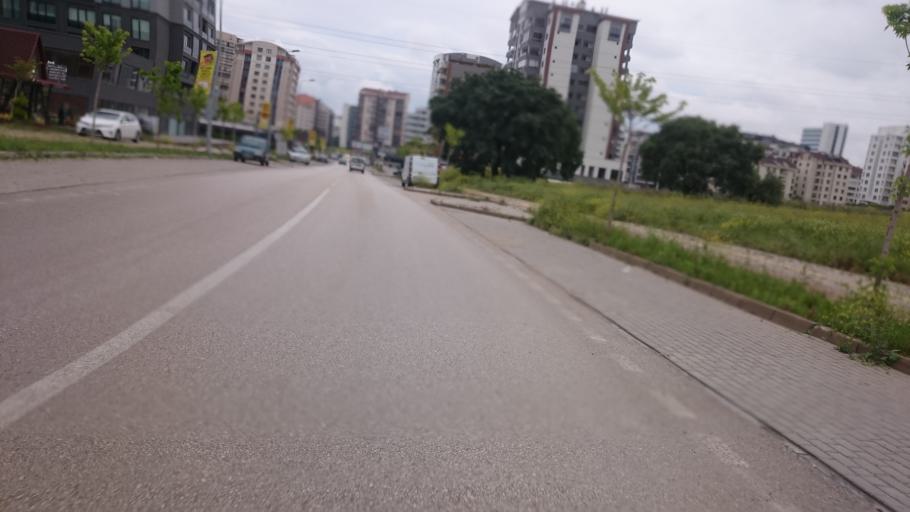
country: TR
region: Bursa
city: Cali
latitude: 40.2165
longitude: 28.9454
